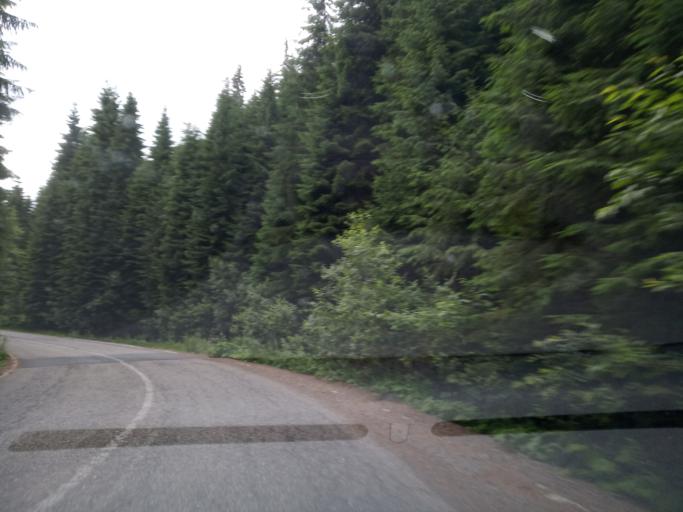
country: RO
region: Valcea
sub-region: Comuna Voineasa
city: Voineasa
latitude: 45.4256
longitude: 23.7389
